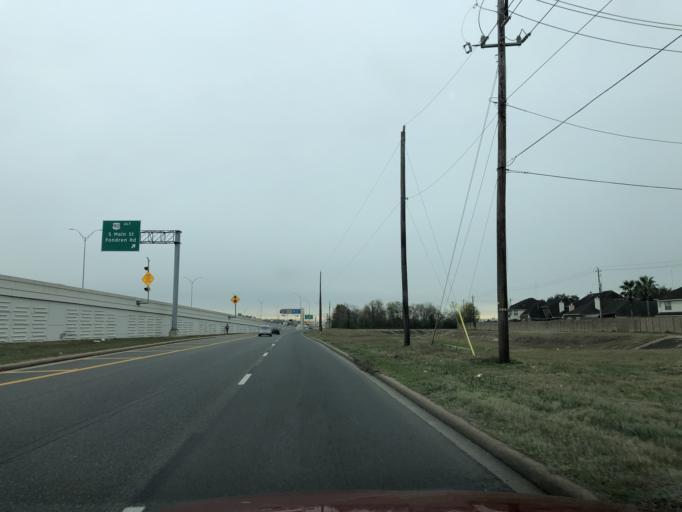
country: US
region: Texas
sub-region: Fort Bend County
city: Missouri City
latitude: 29.6360
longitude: -95.5301
